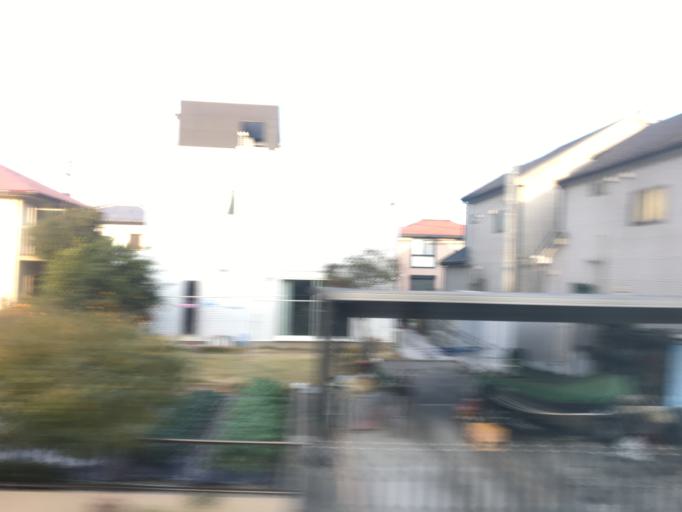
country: JP
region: Saitama
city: Konosu
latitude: 36.0629
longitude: 139.5071
